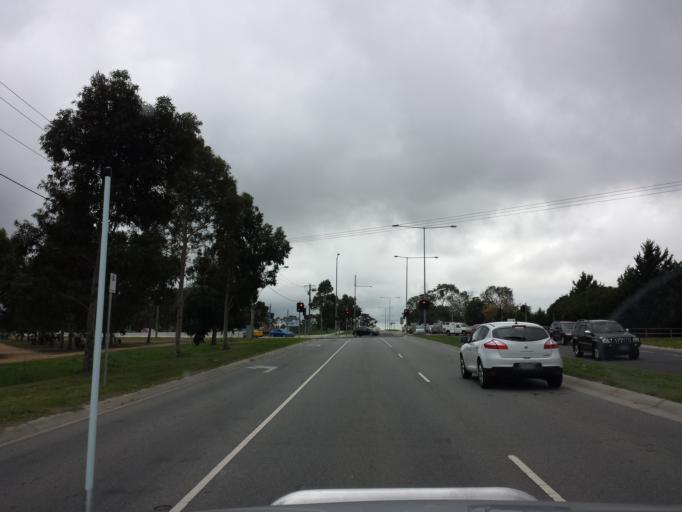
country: AU
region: Victoria
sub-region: Casey
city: Narre Warren South
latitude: -38.0543
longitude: 145.3012
